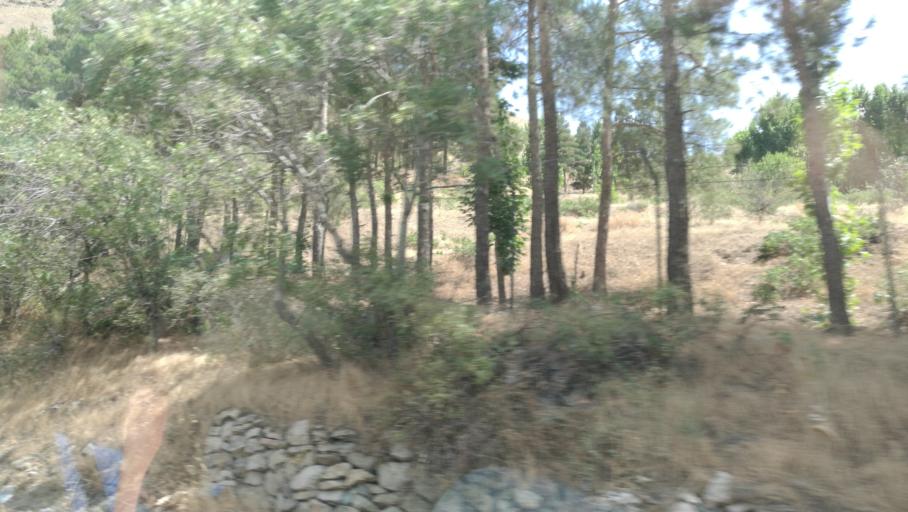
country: IR
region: Alborz
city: Karaj
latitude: 35.9249
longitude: 51.0576
